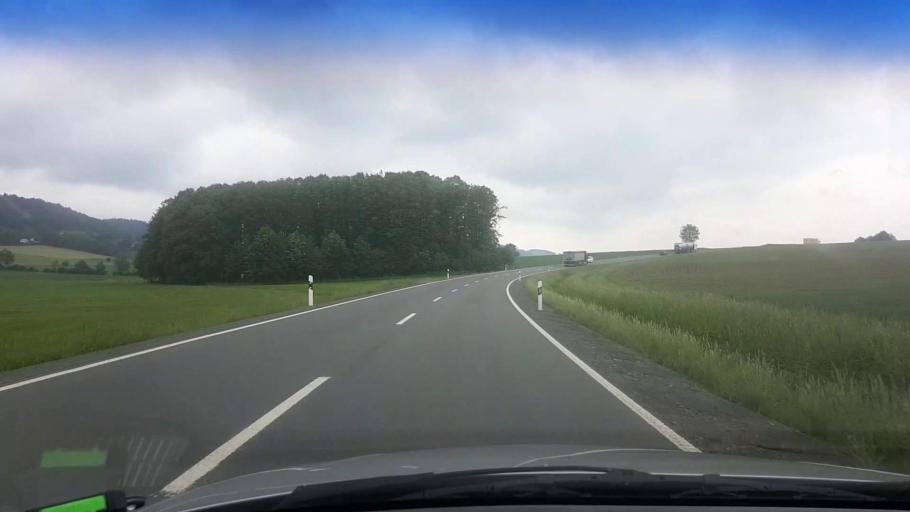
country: DE
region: Bavaria
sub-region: Upper Franconia
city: Gesees
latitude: 50.0237
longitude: 11.6630
